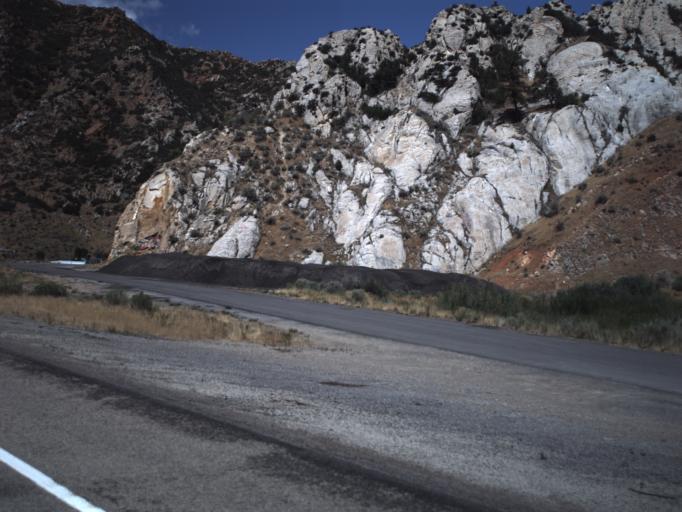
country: US
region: Utah
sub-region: Utah County
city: Woodland Hills
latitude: 39.9940
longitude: -111.4944
